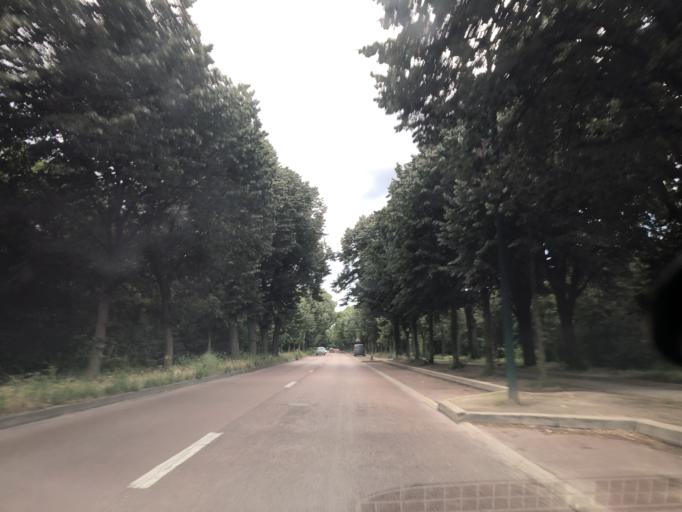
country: FR
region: Ile-de-France
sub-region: Departement du Val-de-Marne
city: Maisons-Alfort
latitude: 48.8301
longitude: 2.4503
